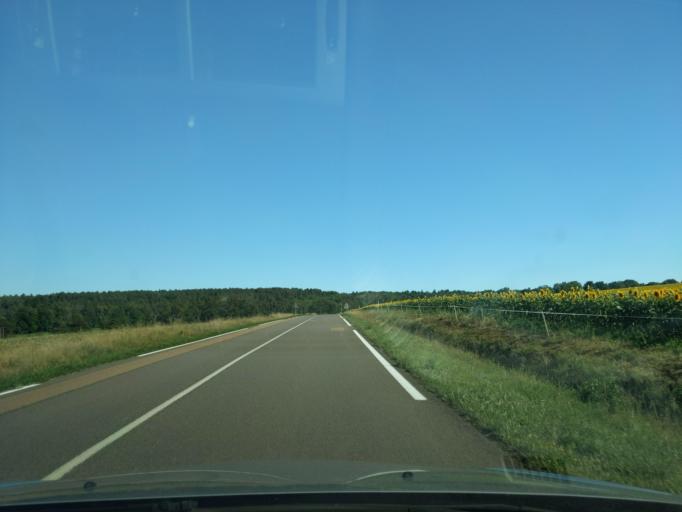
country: FR
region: Bourgogne
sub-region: Departement de la Cote-d'Or
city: Is-sur-Tille
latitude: 47.5134
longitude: 5.0730
